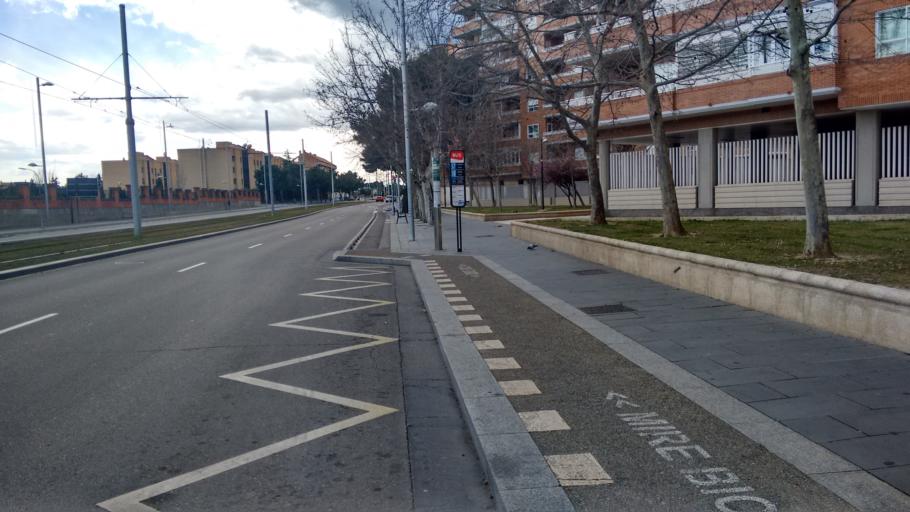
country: ES
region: Aragon
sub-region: Provincia de Zaragoza
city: Delicias
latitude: 41.6316
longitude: -0.9056
